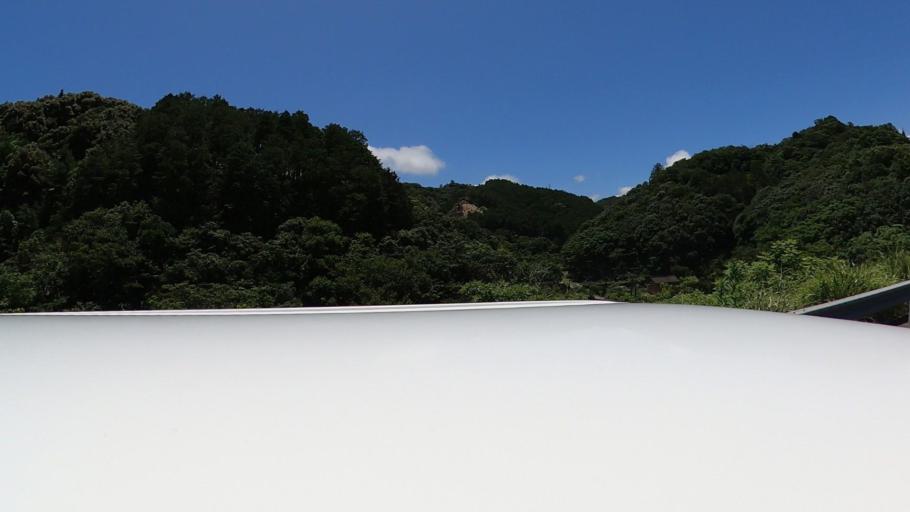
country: JP
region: Miyazaki
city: Nobeoka
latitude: 32.5375
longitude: 131.6601
